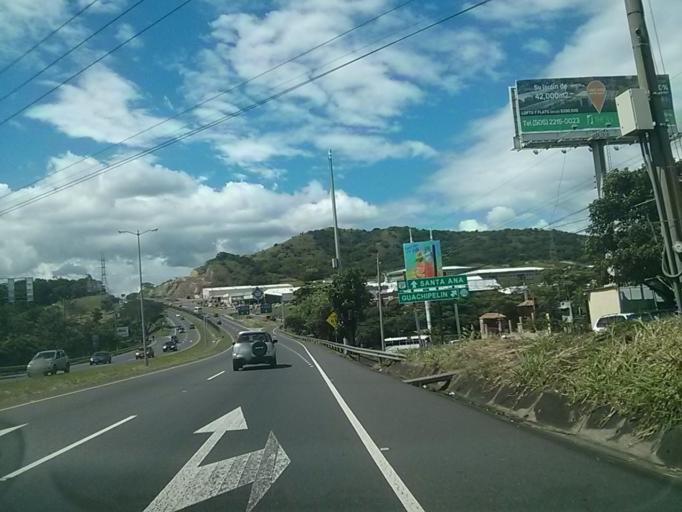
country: CR
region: San Jose
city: Santa Ana
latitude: 9.9480
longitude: -84.1590
